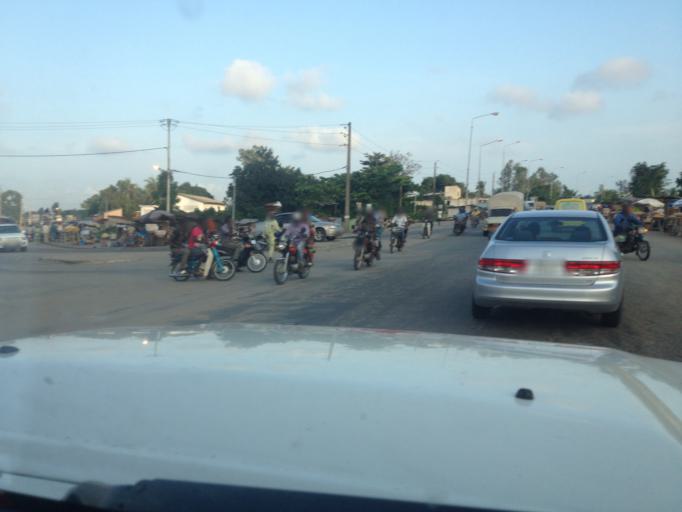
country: BJ
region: Queme
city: Porto-Novo
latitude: 6.4253
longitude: 2.6277
